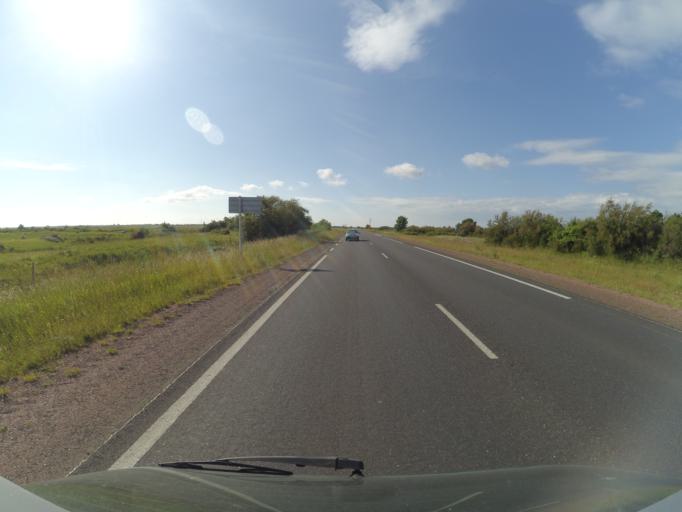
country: FR
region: Poitou-Charentes
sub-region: Departement de la Charente-Maritime
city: Saint-Agnant
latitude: 45.8482
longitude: -0.9549
